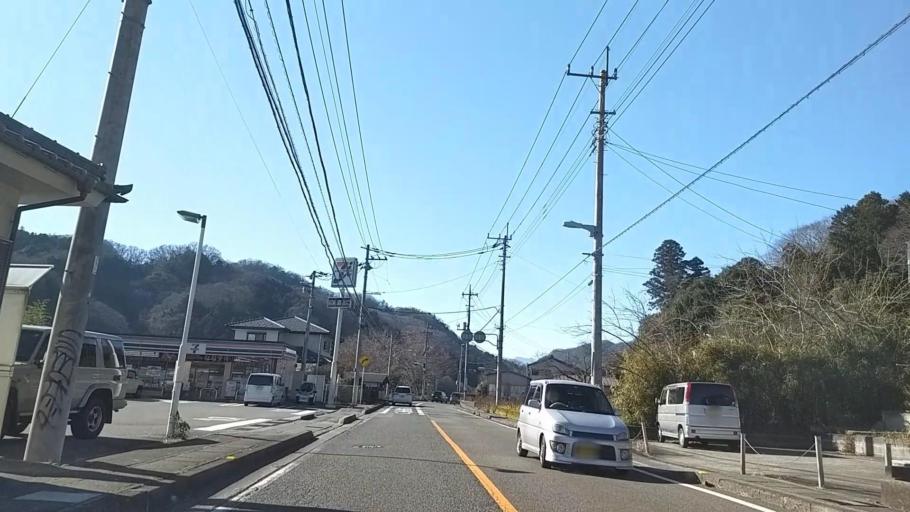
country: JP
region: Yamanashi
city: Uenohara
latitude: 35.6134
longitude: 139.0848
